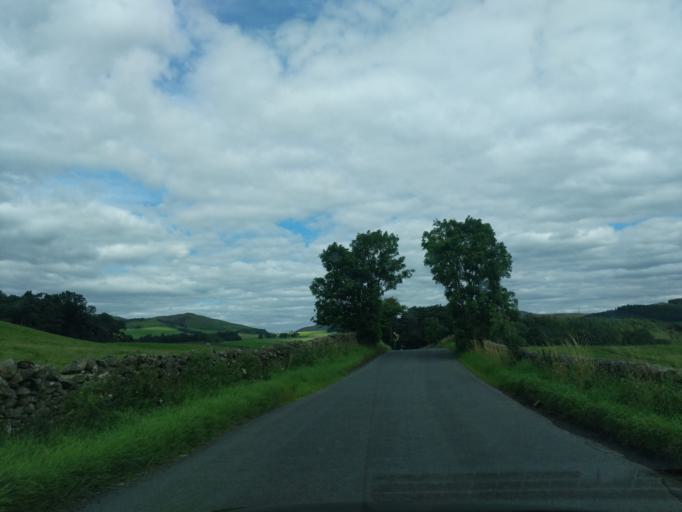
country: GB
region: Scotland
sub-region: The Scottish Borders
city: Peebles
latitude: 55.6435
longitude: -3.2796
